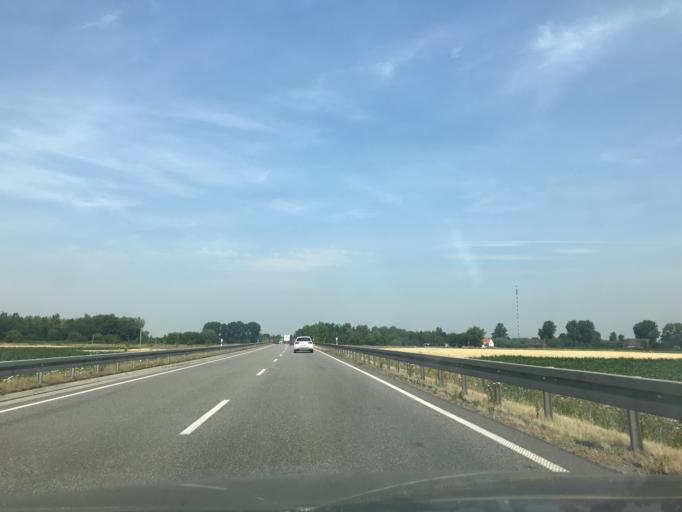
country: DE
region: North Rhine-Westphalia
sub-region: Regierungsbezirk Dusseldorf
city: Alpen
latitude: 51.6234
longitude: 6.5632
